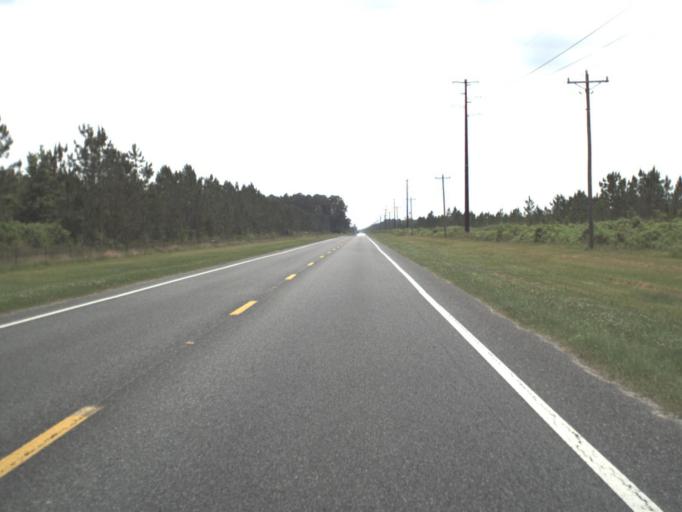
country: US
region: Florida
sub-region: Clay County
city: Middleburg
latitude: 30.0039
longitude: -81.8977
